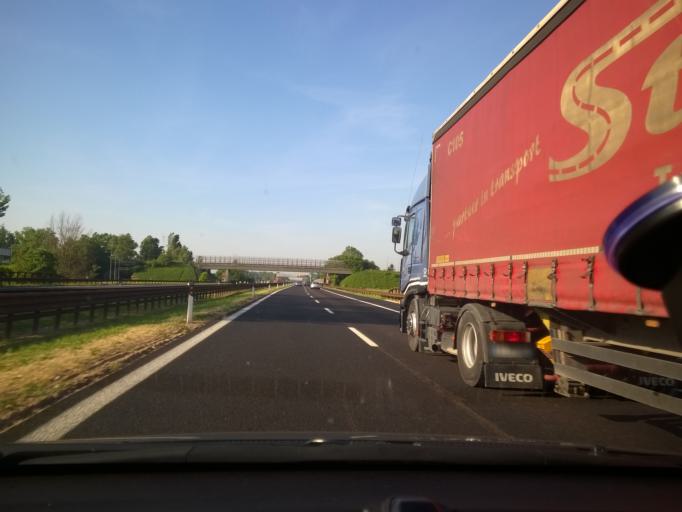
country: IT
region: Emilia-Romagna
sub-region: Provincia di Modena
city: Santa Croce Scuole
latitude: 44.7874
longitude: 10.8509
